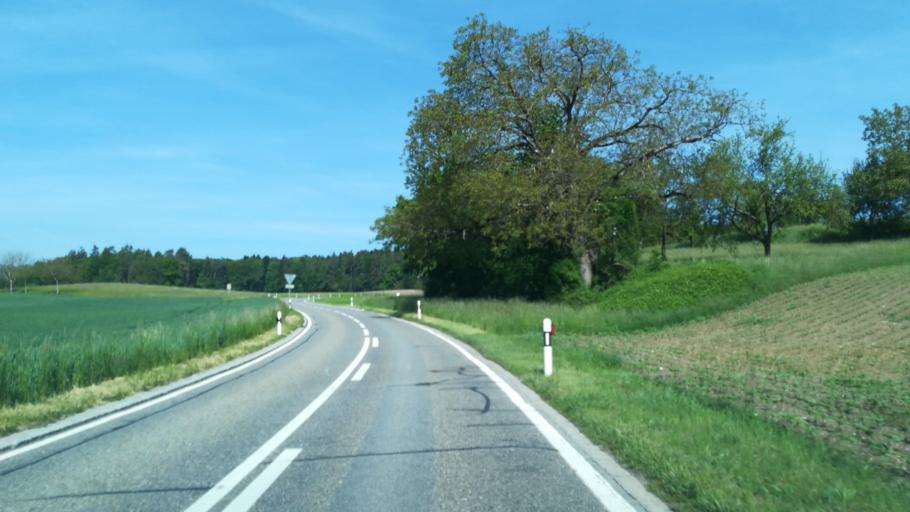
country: CH
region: Thurgau
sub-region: Frauenfeld District
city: Pfyn
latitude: 47.6041
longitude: 8.9450
